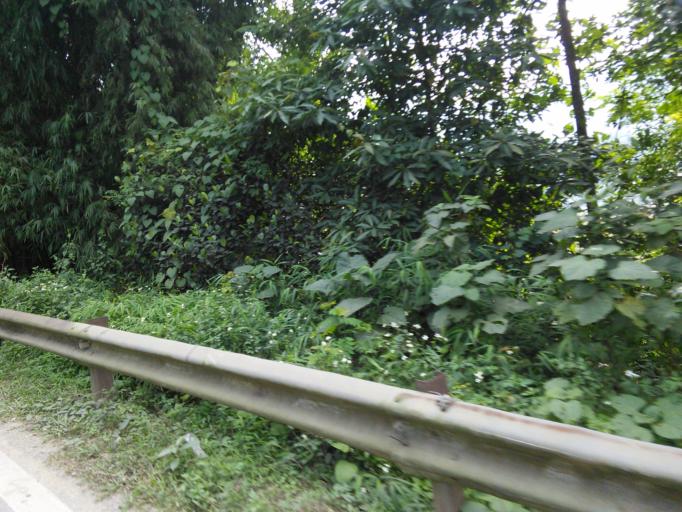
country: VN
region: Lao Cai
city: Lao Cai
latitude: 22.4617
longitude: 103.9480
